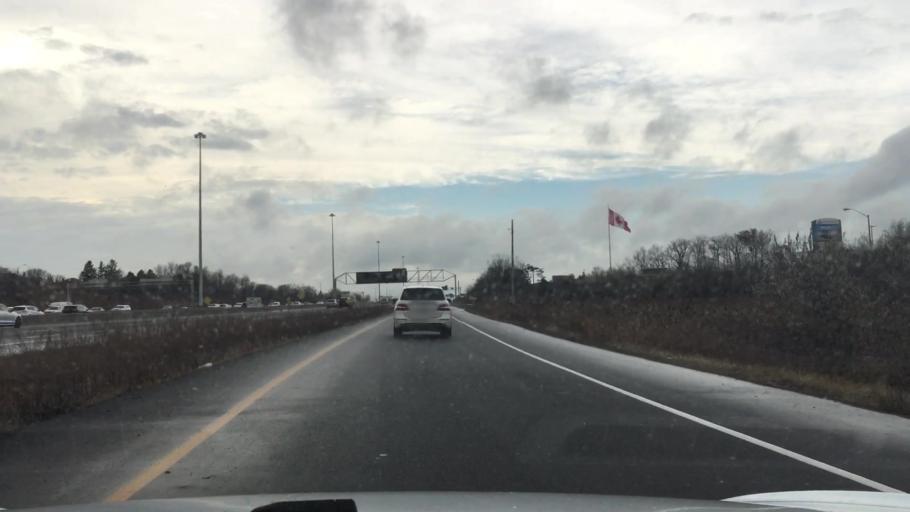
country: CA
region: Ontario
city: Scarborough
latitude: 43.7968
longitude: -79.2006
